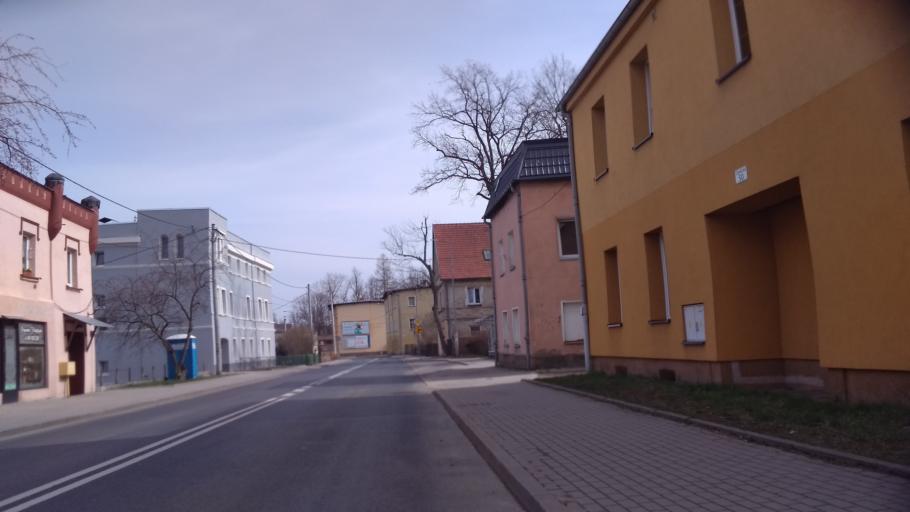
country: PL
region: Lower Silesian Voivodeship
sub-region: Jelenia Gora
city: Cieplice Slaskie Zdroj
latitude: 50.8642
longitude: 15.6715
